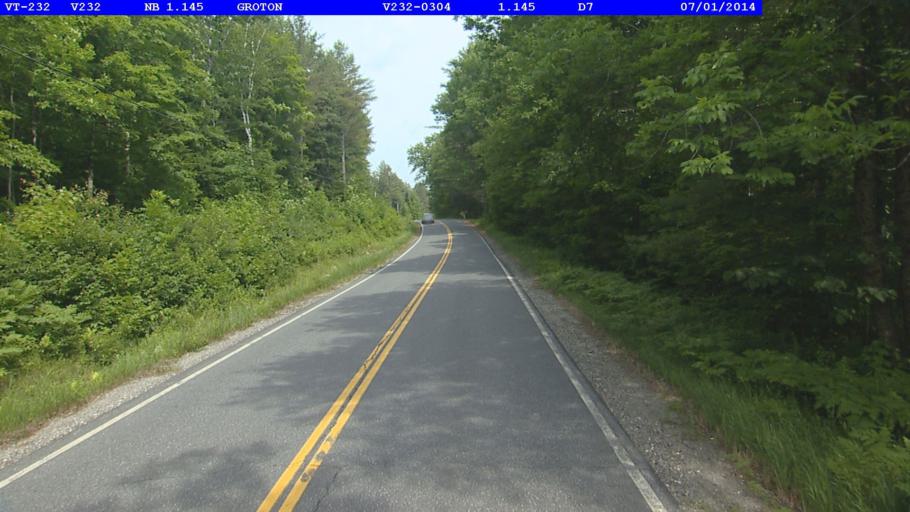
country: US
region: New Hampshire
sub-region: Grafton County
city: Woodsville
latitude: 44.2347
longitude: -72.2337
